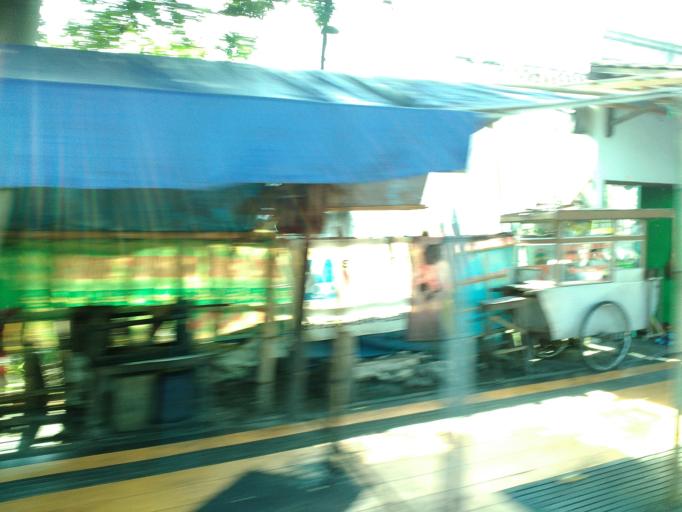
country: ID
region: Central Java
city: Delanggu
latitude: -7.6243
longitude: 110.6972
